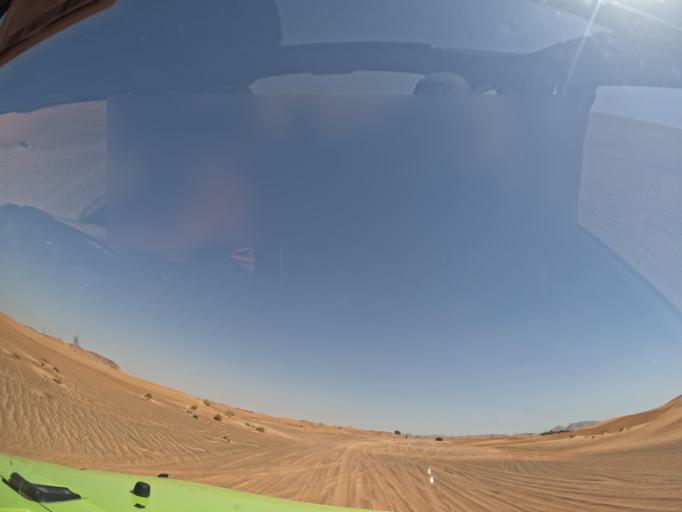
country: AE
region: Ash Shariqah
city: Adh Dhayd
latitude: 25.0028
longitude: 55.7321
